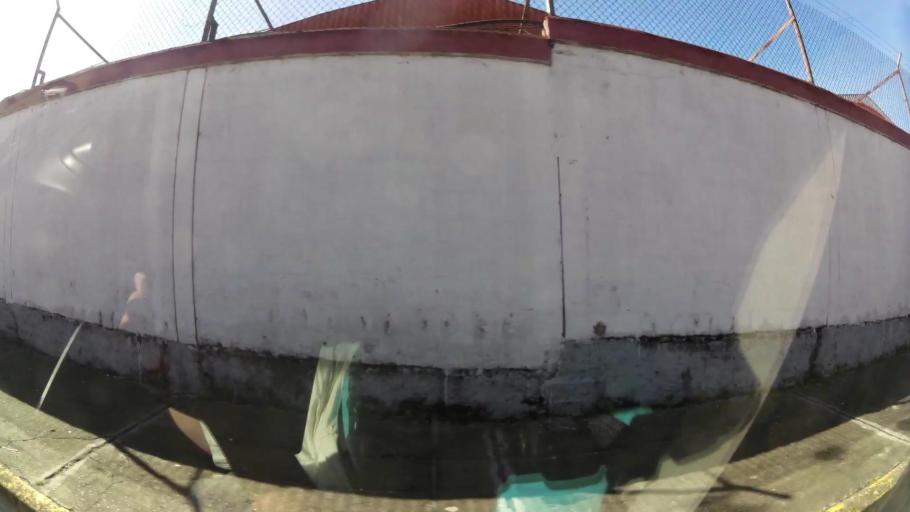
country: EC
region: Pichincha
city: Quito
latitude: -0.2846
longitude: -78.5595
